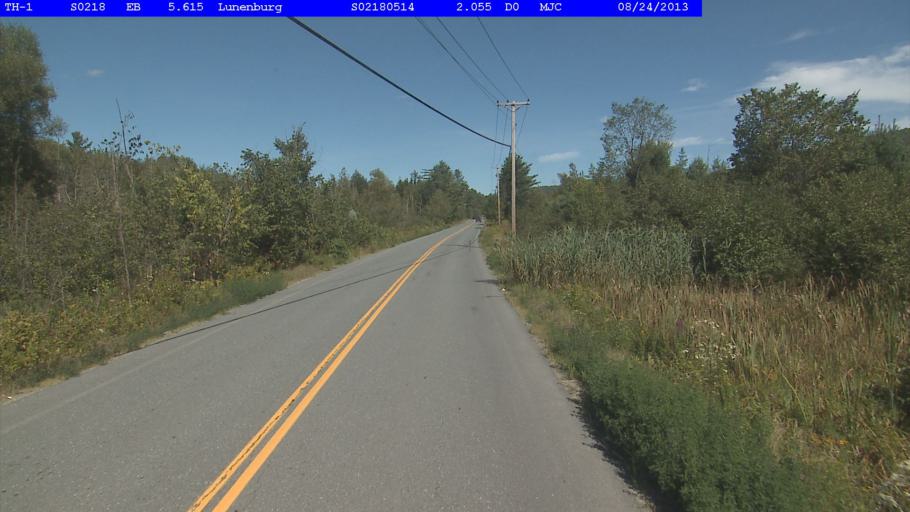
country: US
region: New Hampshire
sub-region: Coos County
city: Whitefield
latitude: 44.4141
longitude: -71.7135
